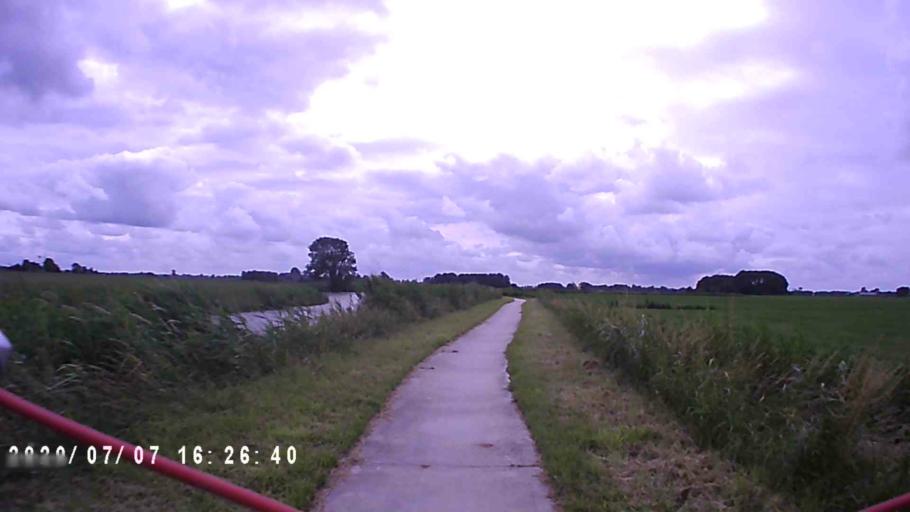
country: NL
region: Groningen
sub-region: Gemeente Winsum
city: Winsum
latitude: 53.3585
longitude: 6.5634
